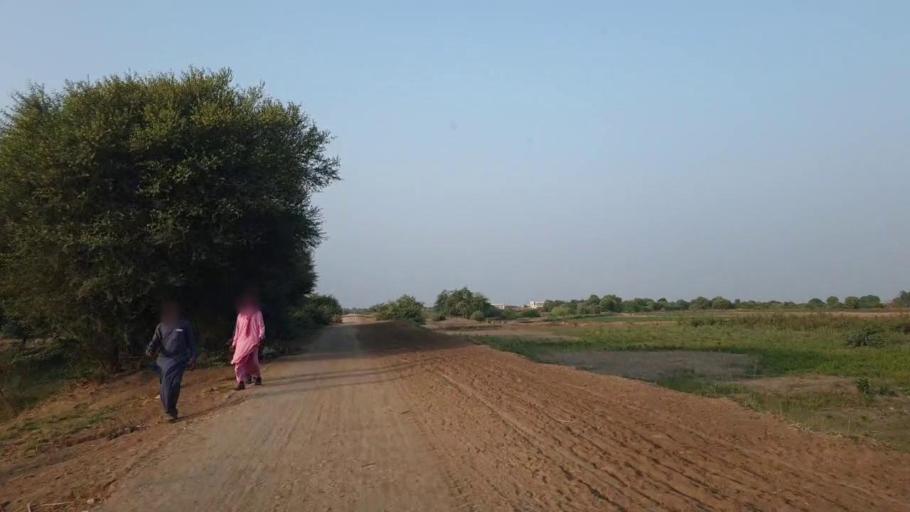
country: PK
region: Sindh
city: Rajo Khanani
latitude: 25.0473
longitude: 68.9644
